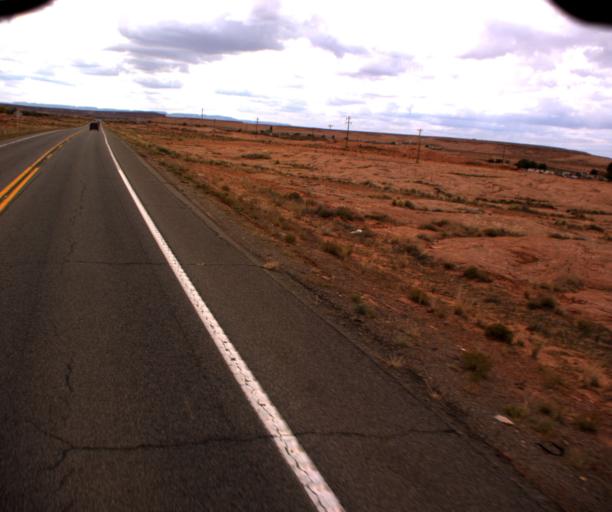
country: US
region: Arizona
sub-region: Navajo County
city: Kayenta
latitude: 36.8344
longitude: -109.8529
